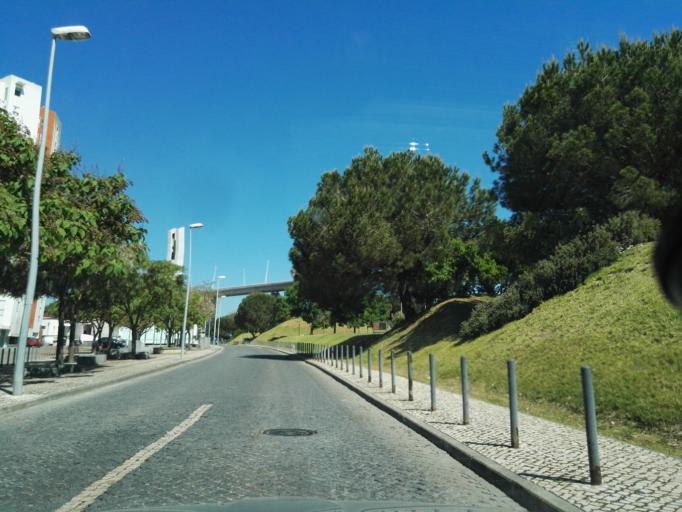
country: PT
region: Lisbon
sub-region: Loures
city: Moscavide
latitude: 38.7840
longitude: -9.0943
